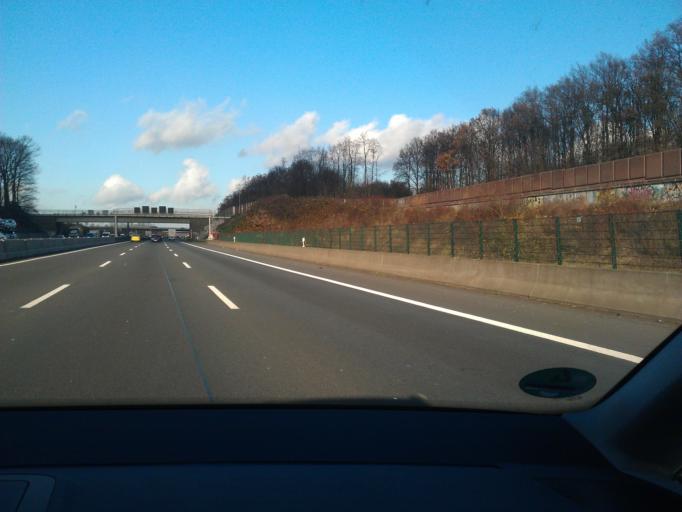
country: DE
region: North Rhine-Westphalia
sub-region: Regierungsbezirk Koln
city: Mengenich
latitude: 50.9460
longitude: 6.8497
